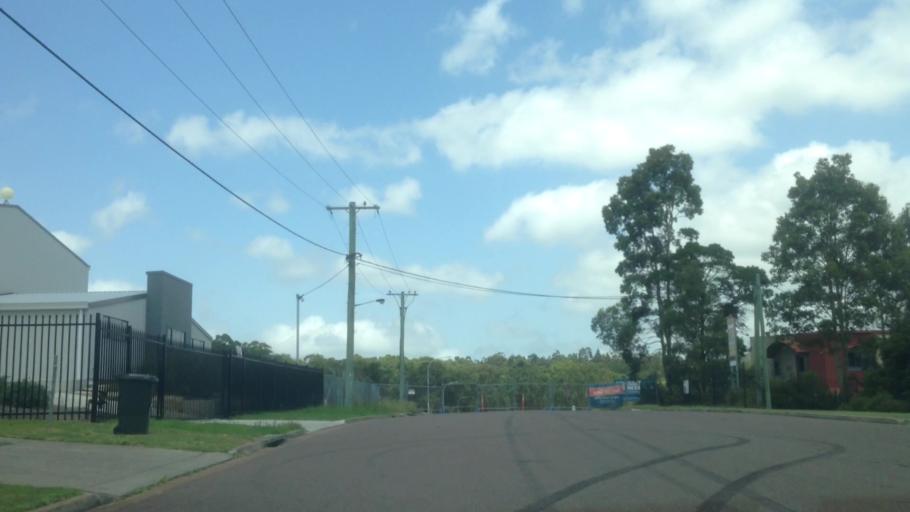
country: AU
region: New South Wales
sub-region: Lake Macquarie Shire
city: Dora Creek
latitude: -33.1203
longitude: 151.4731
